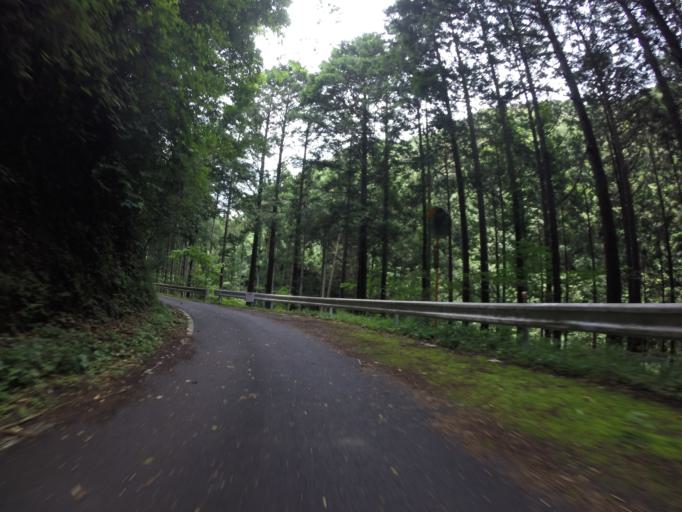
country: JP
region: Shizuoka
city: Shizuoka-shi
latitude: 35.0288
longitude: 138.3029
